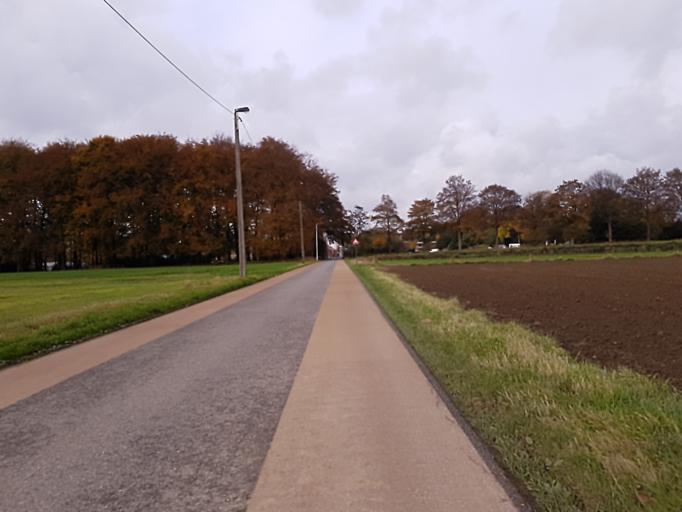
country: BE
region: Flanders
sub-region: Provincie Antwerpen
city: Boechout
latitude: 51.1565
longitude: 4.4996
